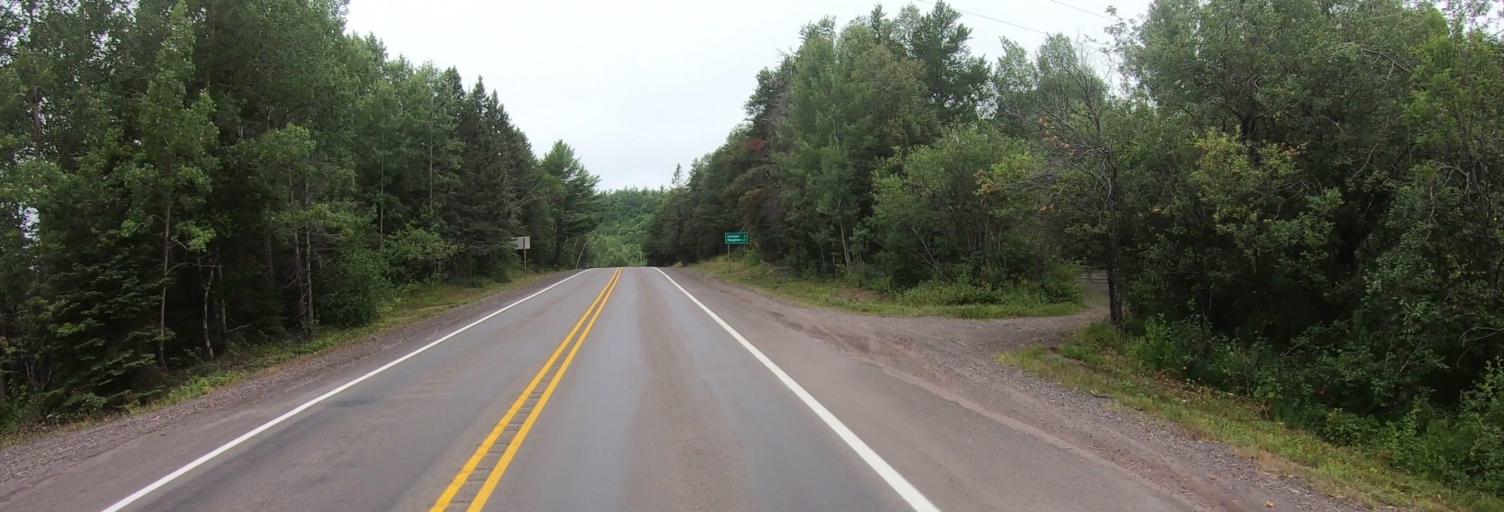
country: US
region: Michigan
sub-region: Keweenaw County
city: Eagle River
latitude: 47.3890
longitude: -88.2791
